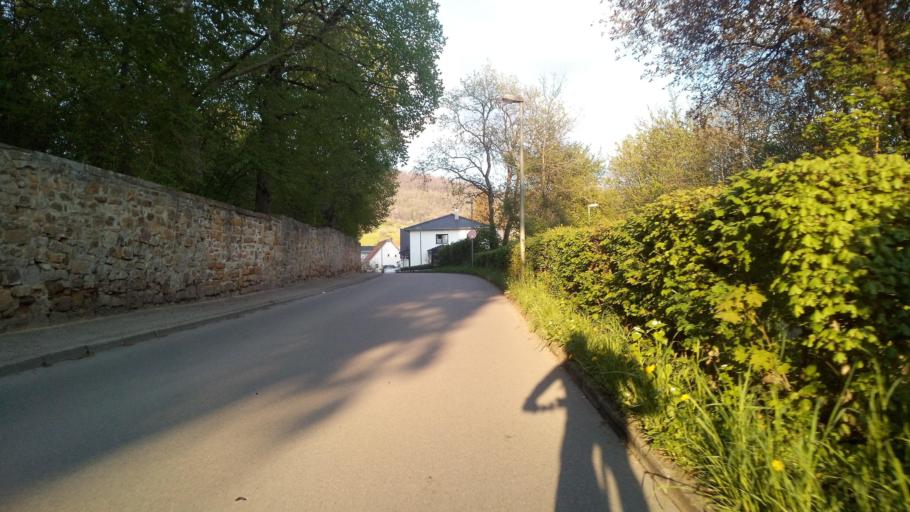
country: DE
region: Baden-Wuerttemberg
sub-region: Regierungsbezirk Stuttgart
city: Donzdorf
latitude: 48.6838
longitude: 9.8086
